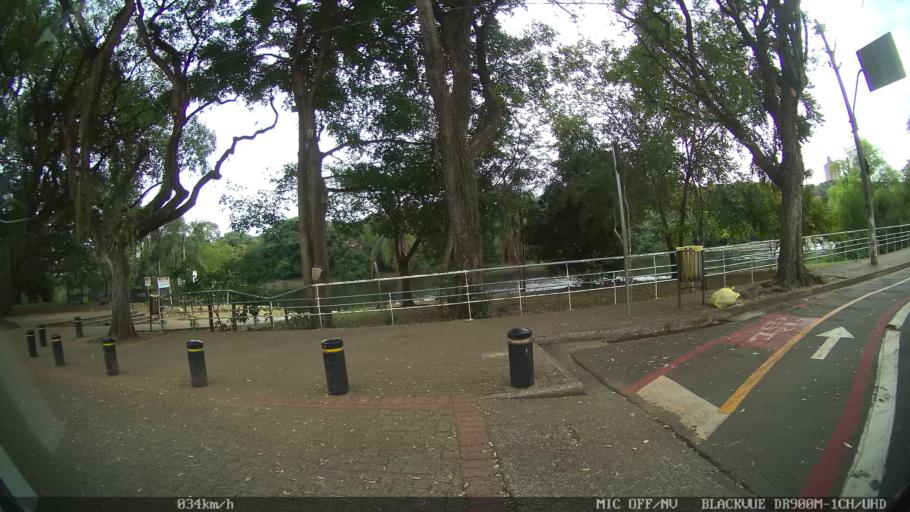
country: BR
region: Sao Paulo
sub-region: Piracicaba
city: Piracicaba
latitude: -22.7218
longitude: -47.6555
